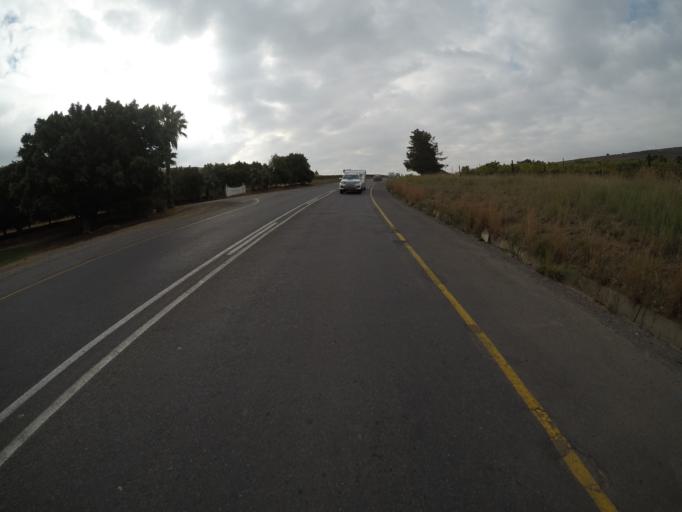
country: ZA
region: Western Cape
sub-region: City of Cape Town
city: Sunset Beach
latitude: -33.8377
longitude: 18.5927
